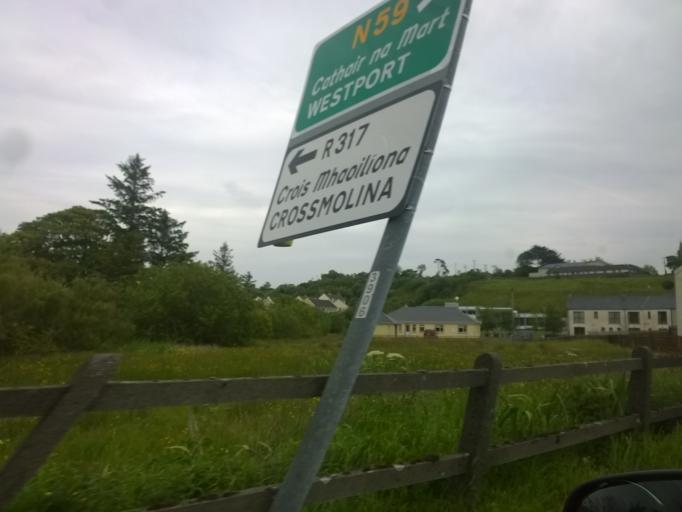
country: IE
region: Connaught
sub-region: Maigh Eo
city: Westport
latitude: 53.8880
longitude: -9.5451
